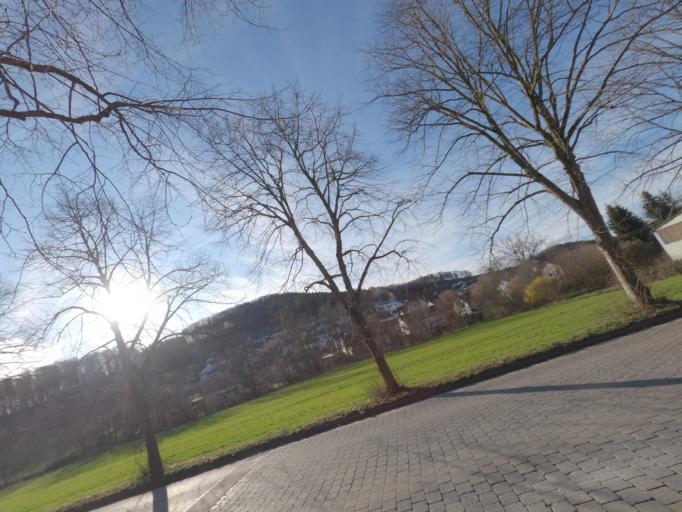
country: DE
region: Baden-Wuerttemberg
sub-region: Regierungsbezirk Stuttgart
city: Donzdorf
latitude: 48.7062
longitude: 9.7982
